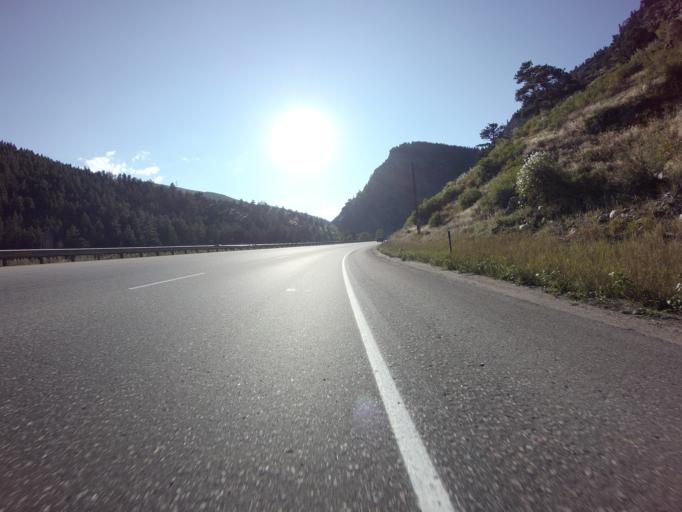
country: US
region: Colorado
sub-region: Clear Creek County
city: Idaho Springs
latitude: 39.7438
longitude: -105.4443
